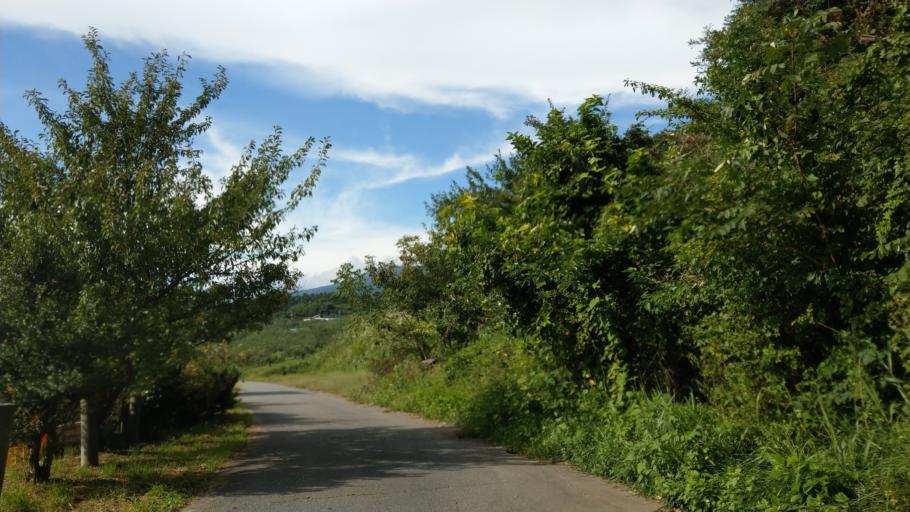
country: JP
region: Nagano
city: Komoro
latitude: 36.3367
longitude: 138.4476
